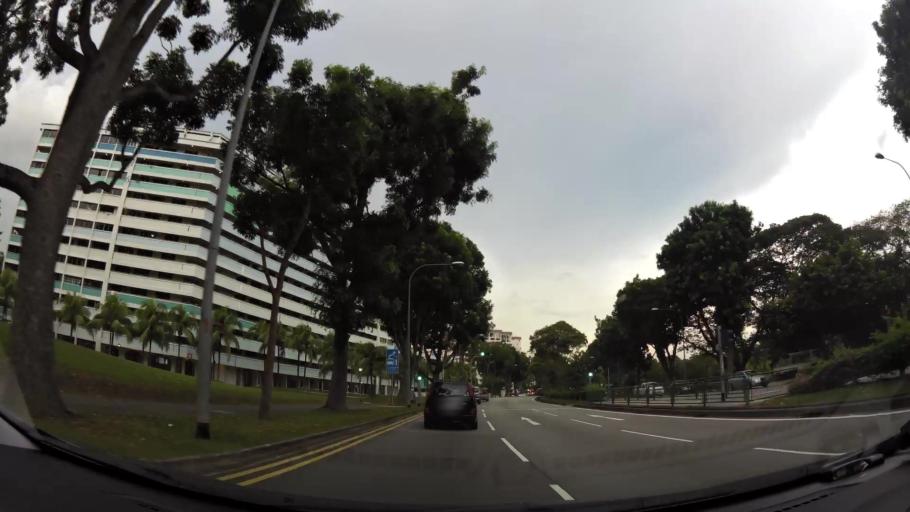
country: MY
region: Johor
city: Kampung Pasir Gudang Baru
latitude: 1.4112
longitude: 103.8331
